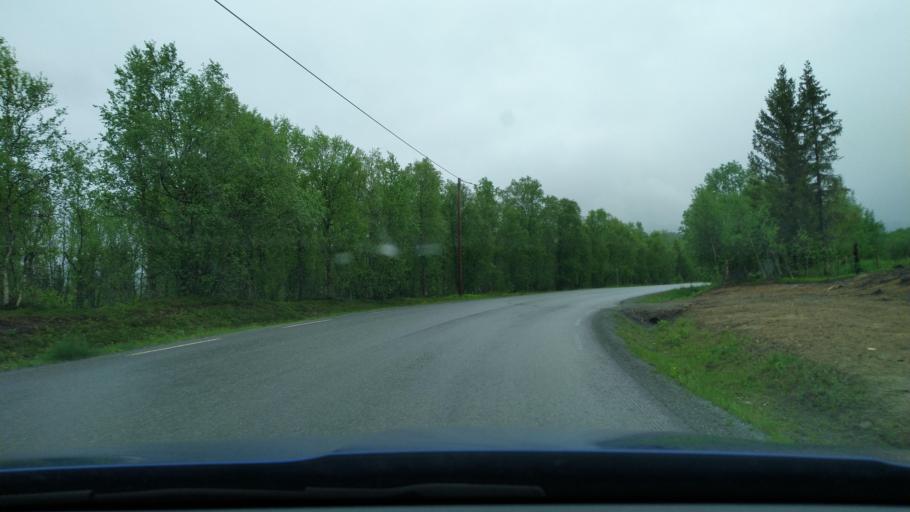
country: NO
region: Troms
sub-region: Dyroy
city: Brostadbotn
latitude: 69.0805
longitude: 17.6995
